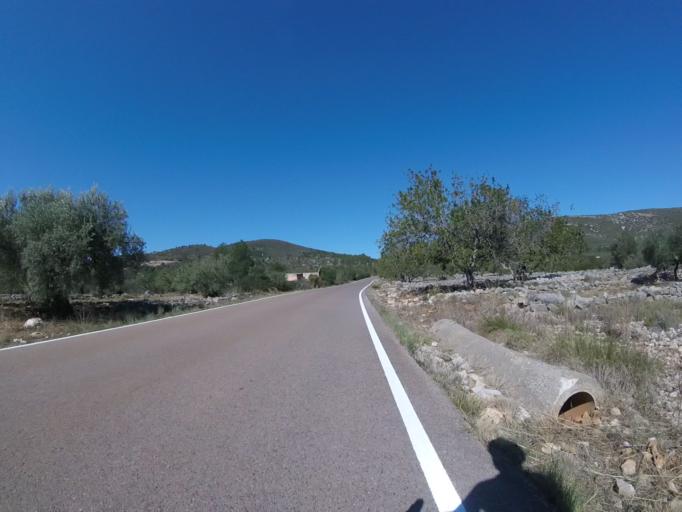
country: ES
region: Valencia
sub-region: Provincia de Castello
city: Santa Magdalena de Pulpis
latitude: 40.3803
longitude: 0.2659
